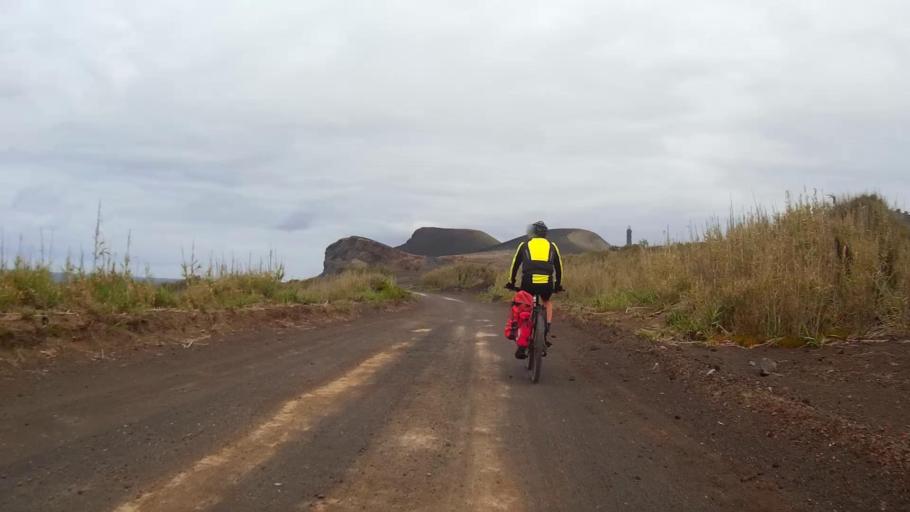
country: PT
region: Azores
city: Ribeira Grande
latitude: 38.5911
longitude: -28.8240
